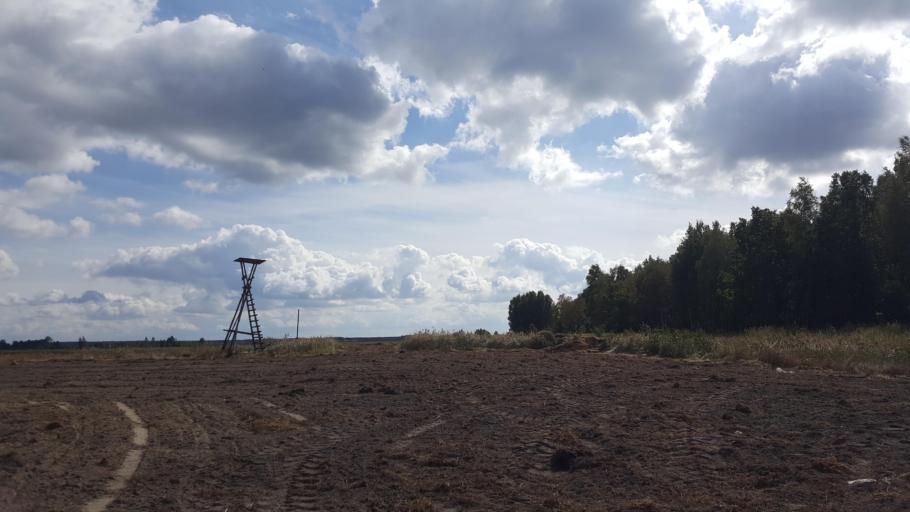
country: BY
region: Brest
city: Kamyanyets
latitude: 52.4599
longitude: 23.9303
